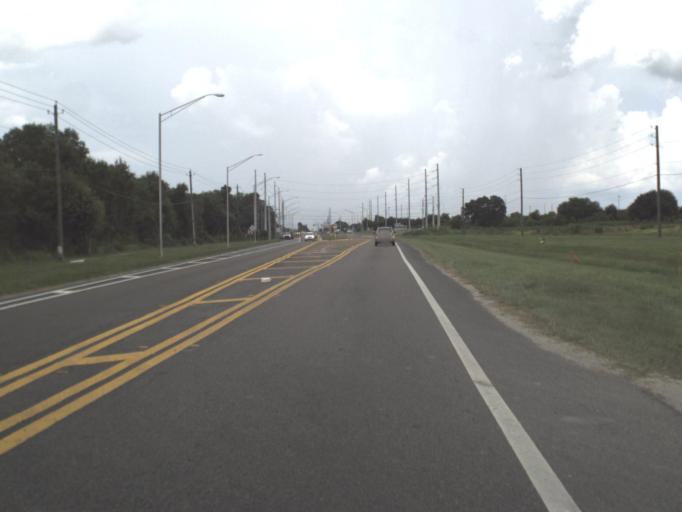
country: US
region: Florida
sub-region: Hillsborough County
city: Sun City Center
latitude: 27.7125
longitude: -82.3278
